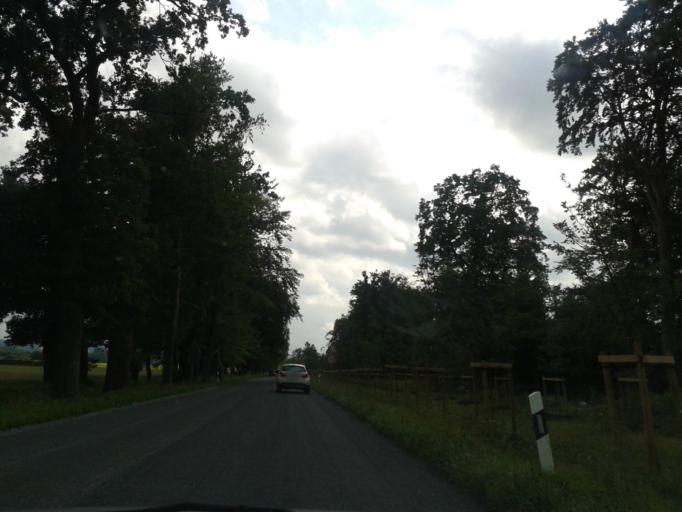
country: DE
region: North Rhine-Westphalia
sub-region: Regierungsbezirk Detmold
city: Schlangen
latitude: 51.8364
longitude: 8.8442
